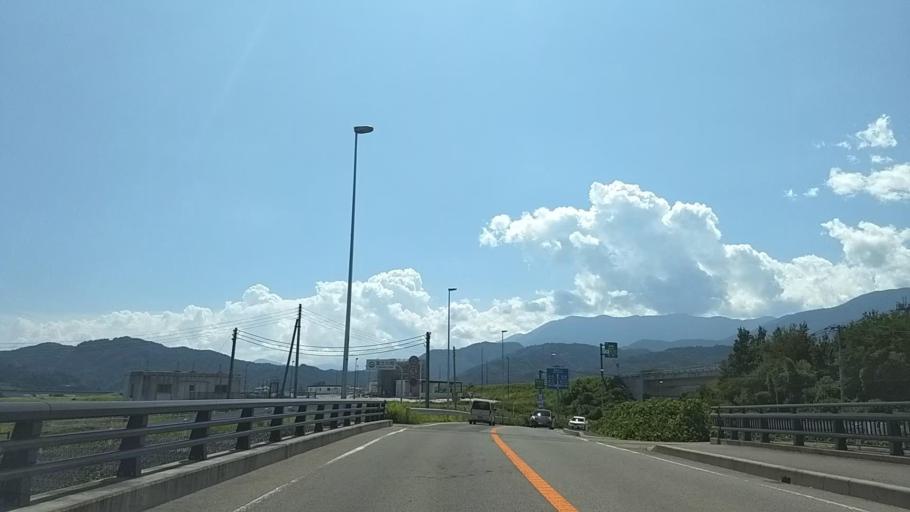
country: JP
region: Yamanashi
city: Ryuo
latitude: 35.5663
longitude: 138.4747
